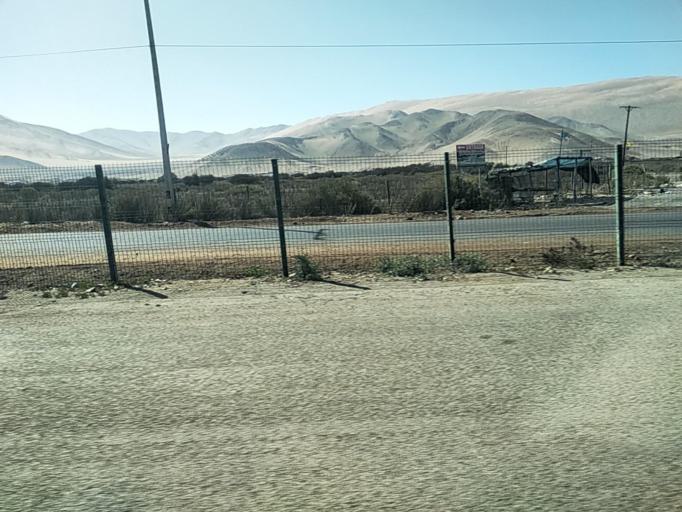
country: CL
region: Atacama
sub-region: Provincia de Copiapo
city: Copiapo
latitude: -27.2959
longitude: -70.4747
